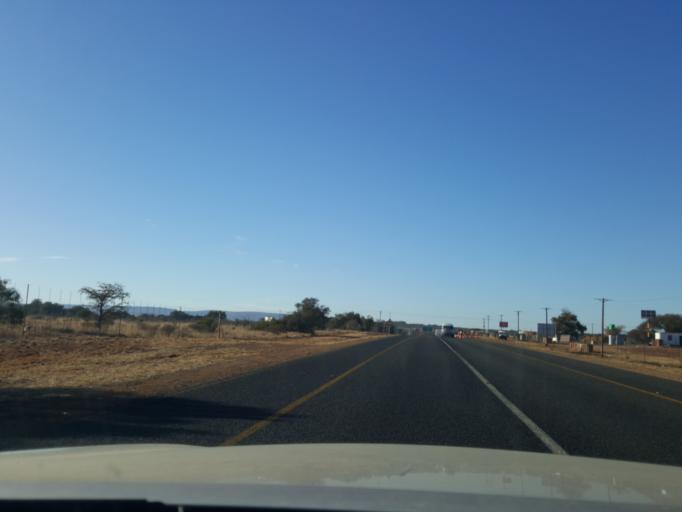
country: ZA
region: North-West
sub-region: Ngaka Modiri Molema District Municipality
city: Zeerust
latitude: -25.5582
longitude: 26.0604
